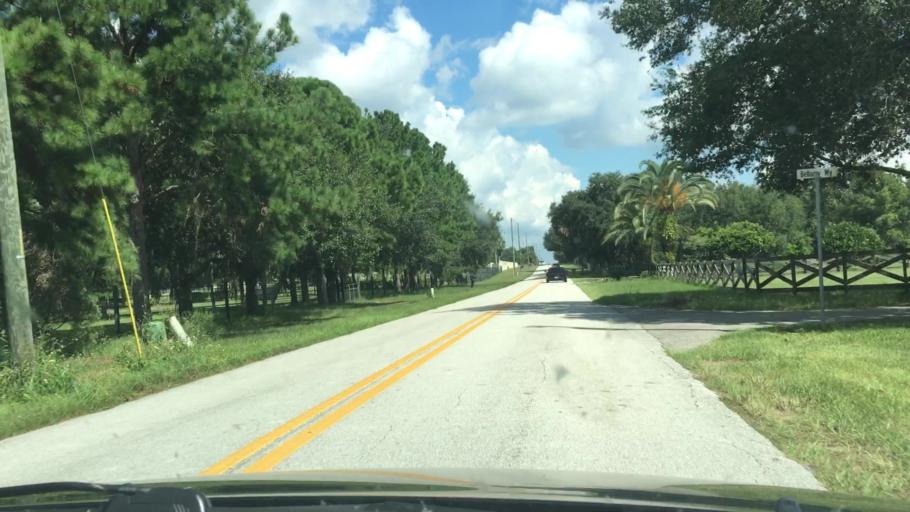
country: US
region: Florida
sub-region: Lake County
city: Montverde
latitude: 28.5978
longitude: -81.6902
